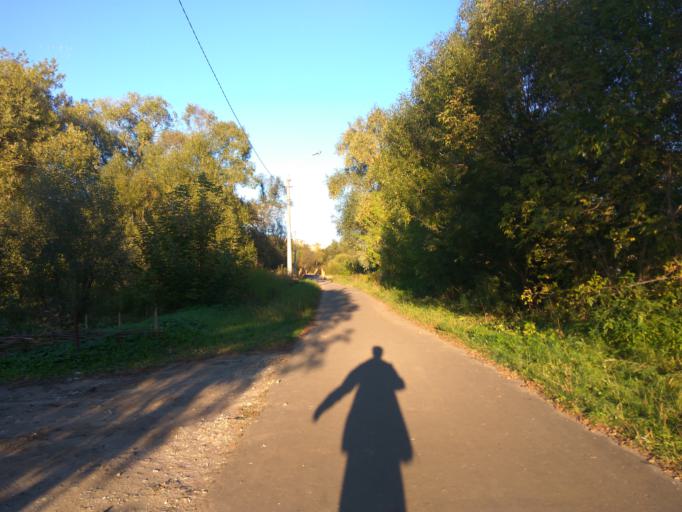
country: RU
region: Moskovskaya
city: Yegor'yevsk
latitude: 55.3721
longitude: 39.0375
